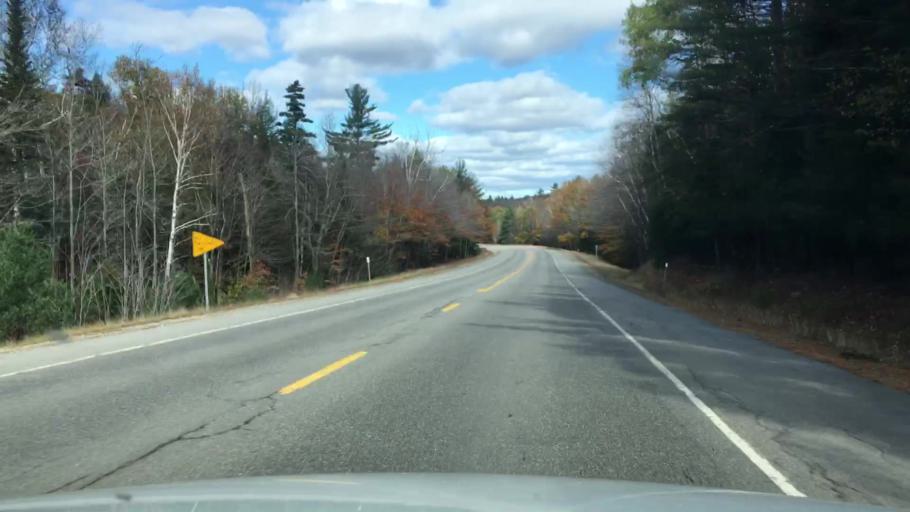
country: US
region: New Hampshire
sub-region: Coos County
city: Gorham
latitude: 44.3139
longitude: -71.2180
